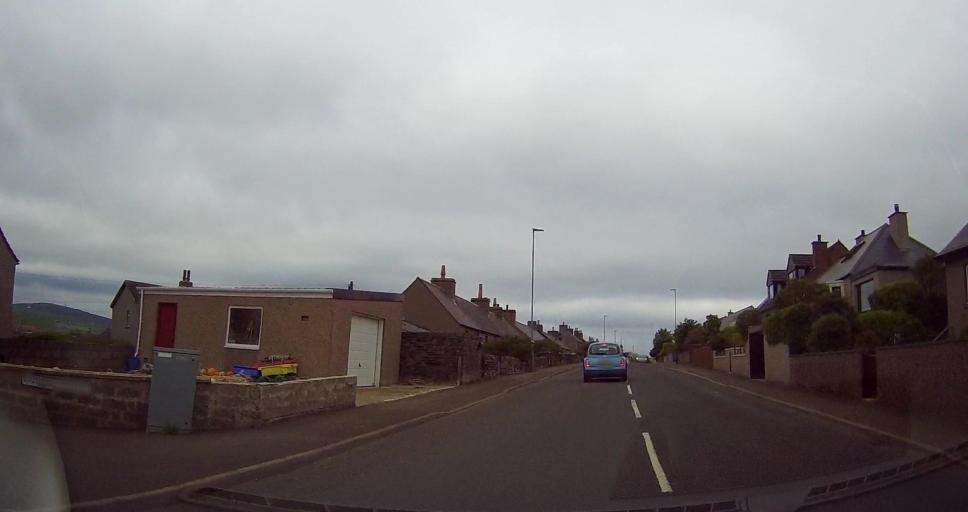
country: GB
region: Scotland
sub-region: Orkney Islands
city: Kirkwall
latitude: 58.9736
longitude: -2.9532
